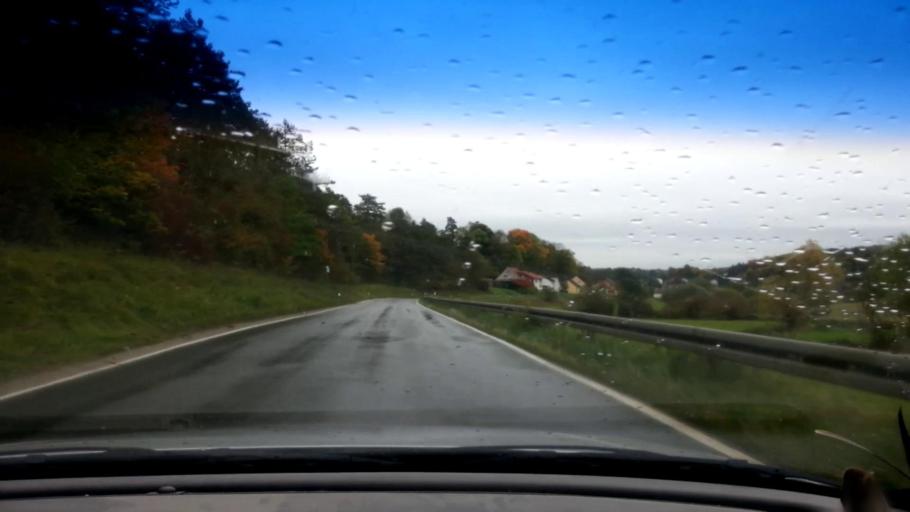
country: DE
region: Bavaria
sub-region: Upper Franconia
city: Heiligenstadt
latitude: 49.8732
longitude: 11.1493
